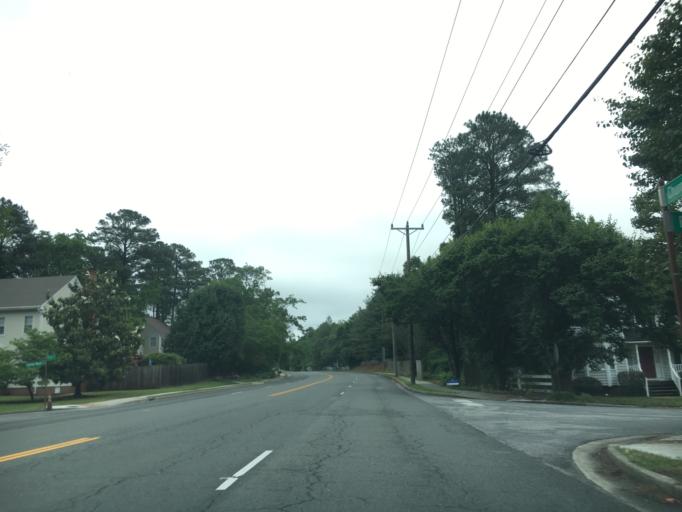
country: US
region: Virginia
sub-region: Henrico County
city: Short Pump
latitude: 37.6320
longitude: -77.6227
